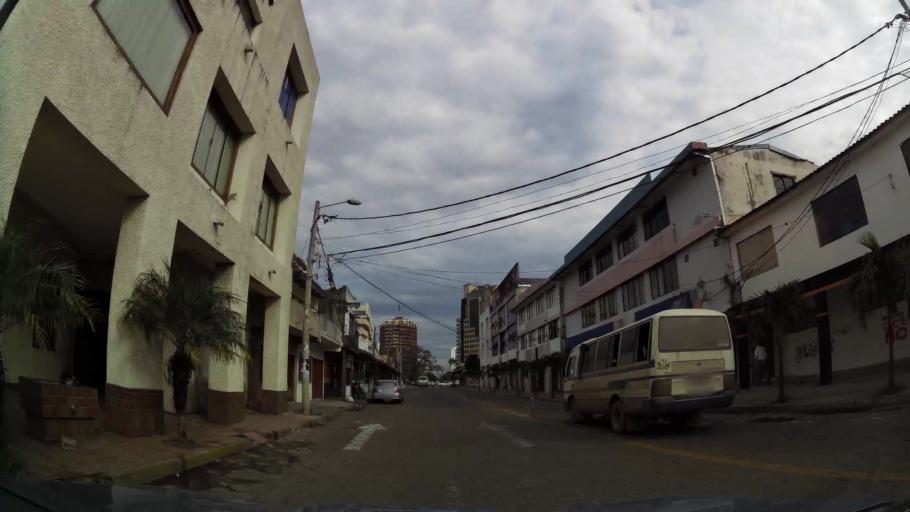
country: BO
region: Santa Cruz
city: Santa Cruz de la Sierra
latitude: -17.7880
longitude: -63.1774
